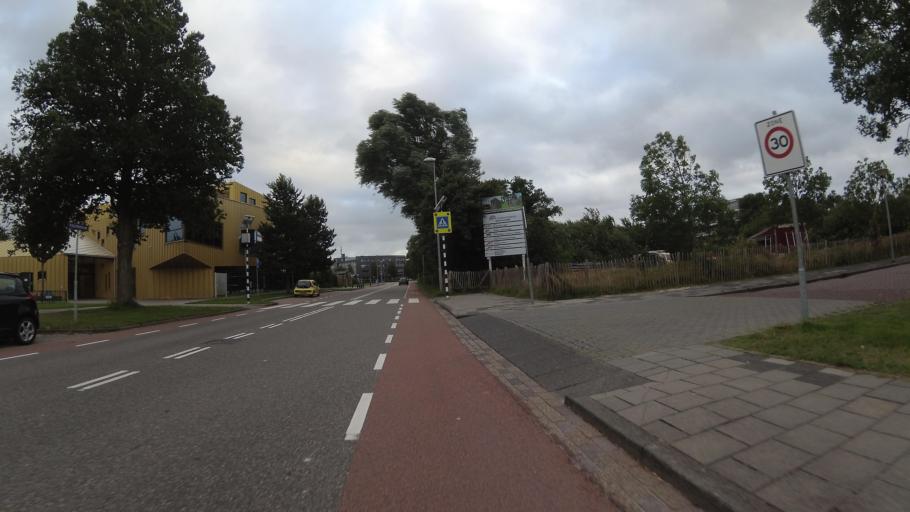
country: NL
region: North Holland
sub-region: Gemeente Den Helder
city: Den Helder
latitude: 52.9402
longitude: 4.7445
